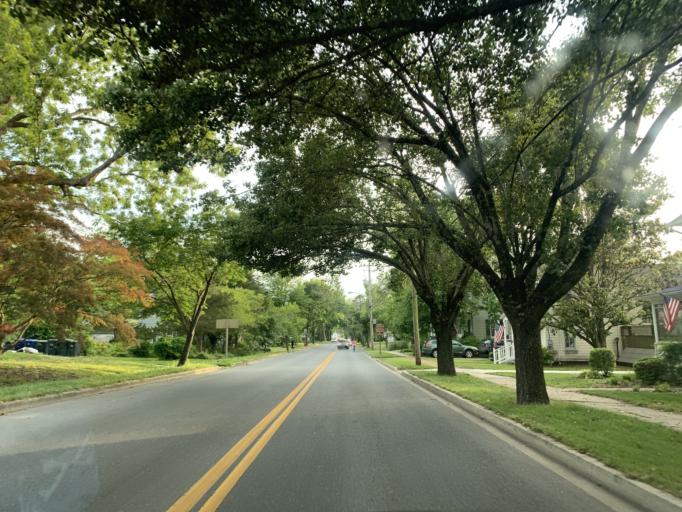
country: US
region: Maryland
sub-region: Worcester County
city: Snow Hill
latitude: 38.1758
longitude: -75.3957
